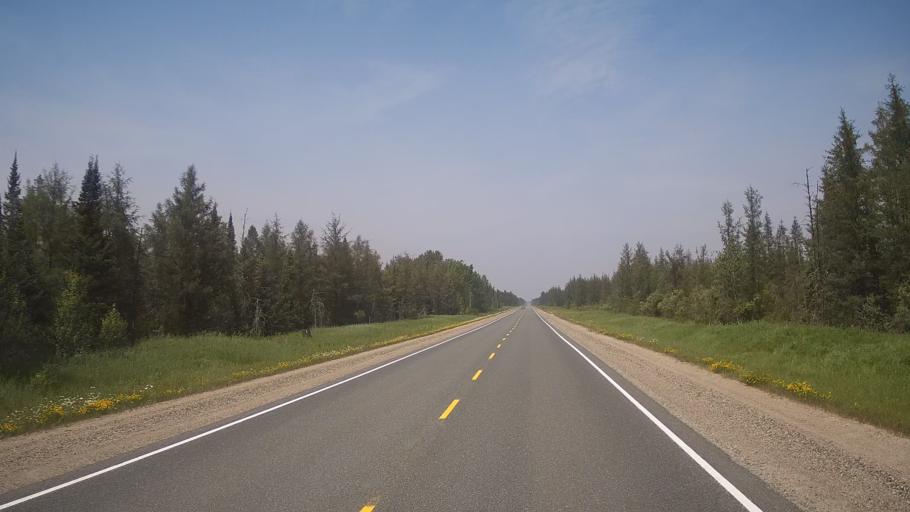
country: CA
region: Ontario
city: Timmins
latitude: 48.8301
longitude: -81.3720
